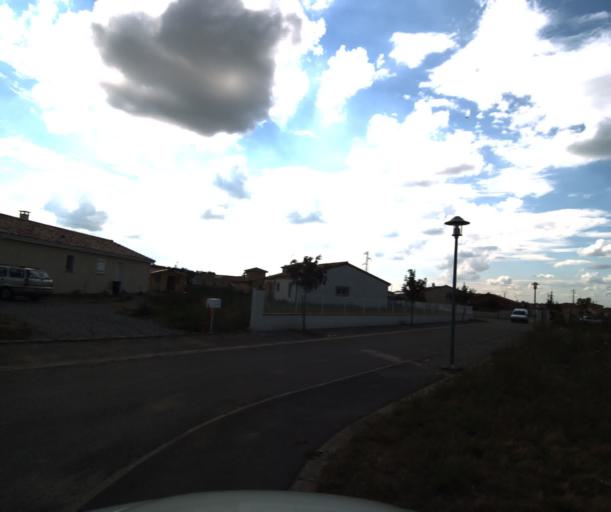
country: FR
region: Midi-Pyrenees
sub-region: Departement de la Haute-Garonne
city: Saubens
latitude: 43.4780
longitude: 1.3580
